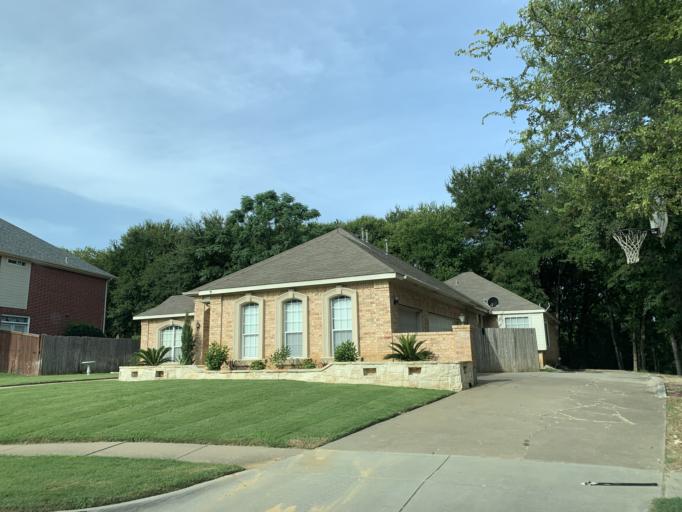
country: US
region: Texas
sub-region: Dallas County
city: Grand Prairie
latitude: 32.6705
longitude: -97.0030
